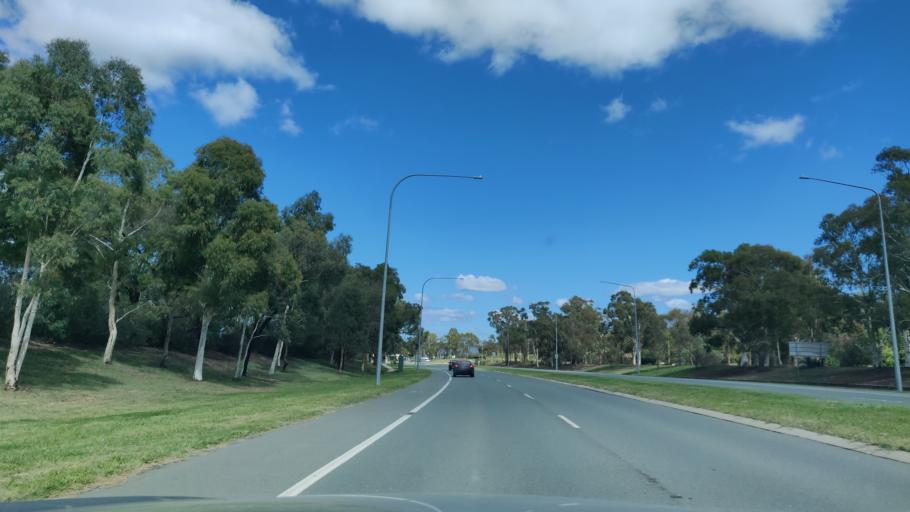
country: AU
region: Australian Capital Territory
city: Macarthur
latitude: -35.4008
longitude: 149.0658
